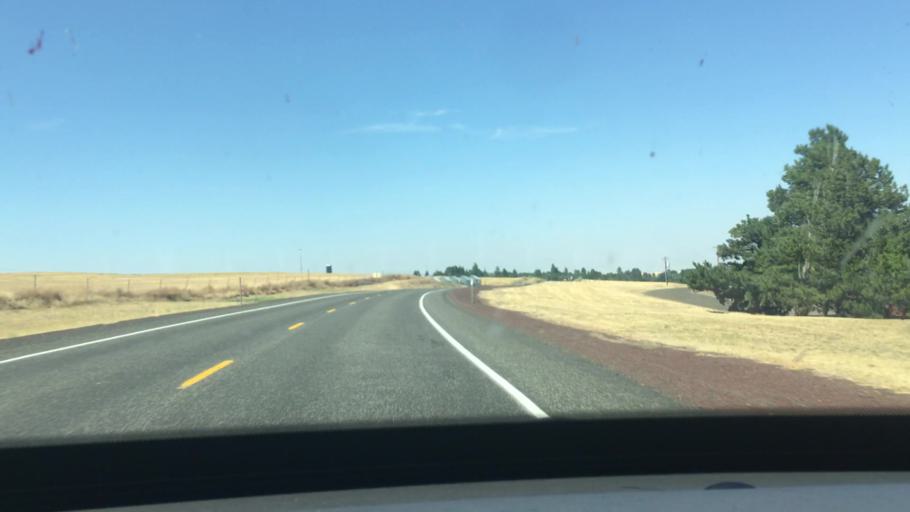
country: US
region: Oregon
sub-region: Sherman County
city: Moro
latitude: 45.4722
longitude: -120.7447
